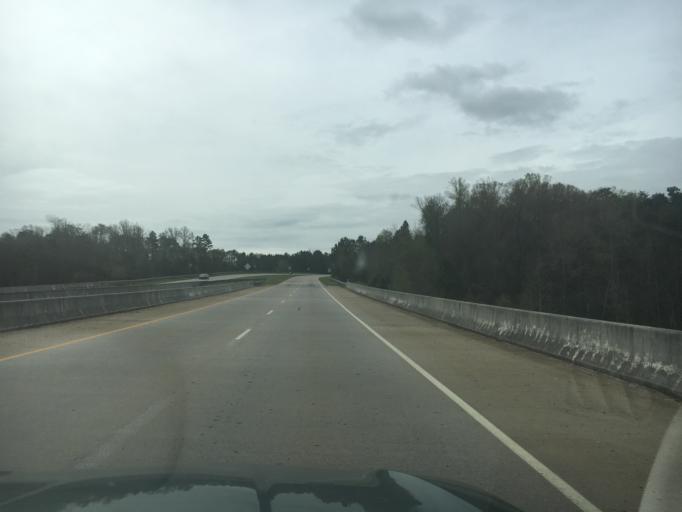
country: US
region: South Carolina
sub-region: Spartanburg County
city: Duncan
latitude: 34.9497
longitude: -82.1797
